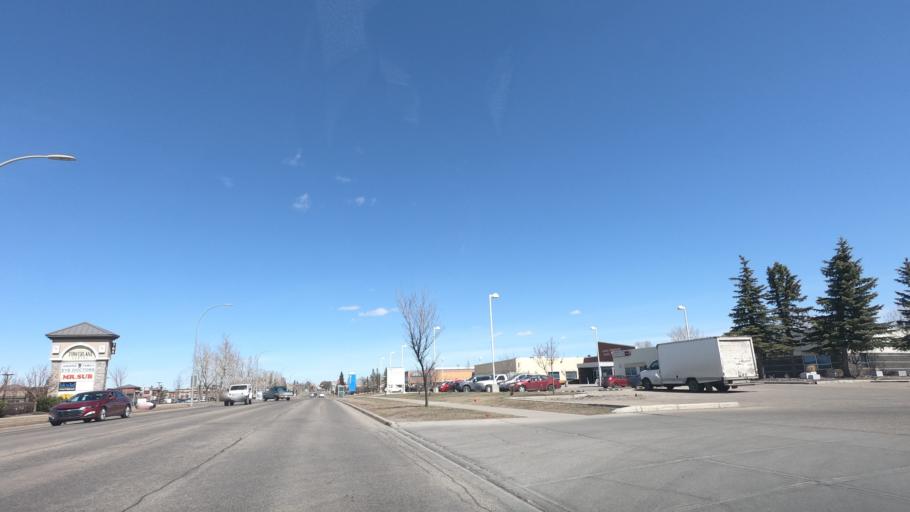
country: CA
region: Alberta
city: Airdrie
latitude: 51.2864
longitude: -114.0133
